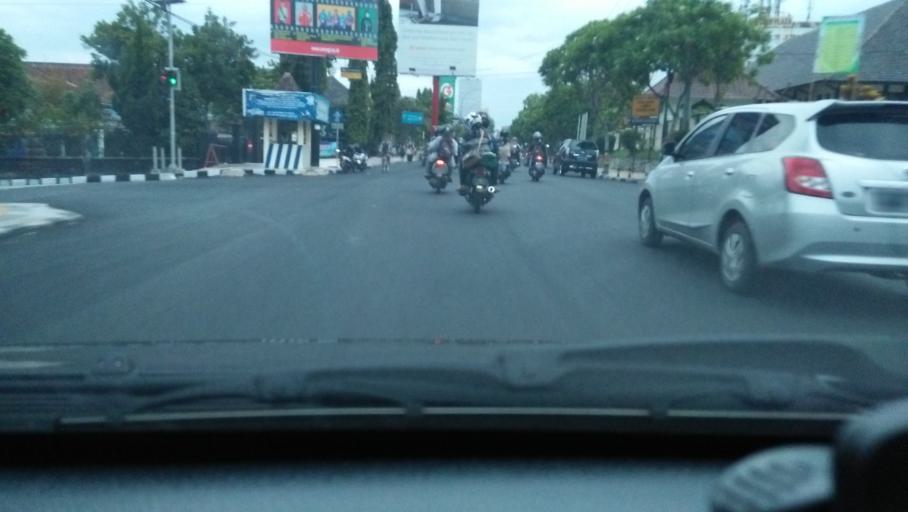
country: ID
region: Central Java
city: Magelang
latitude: -7.4743
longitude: 110.2183
